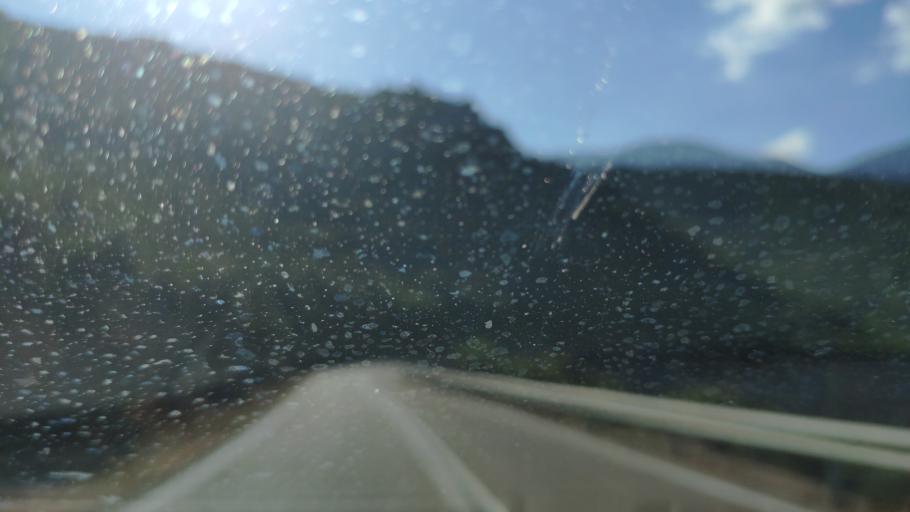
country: GR
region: West Greece
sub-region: Nomos Aitolias kai Akarnanias
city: Archontochorion
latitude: 38.6987
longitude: 21.0796
